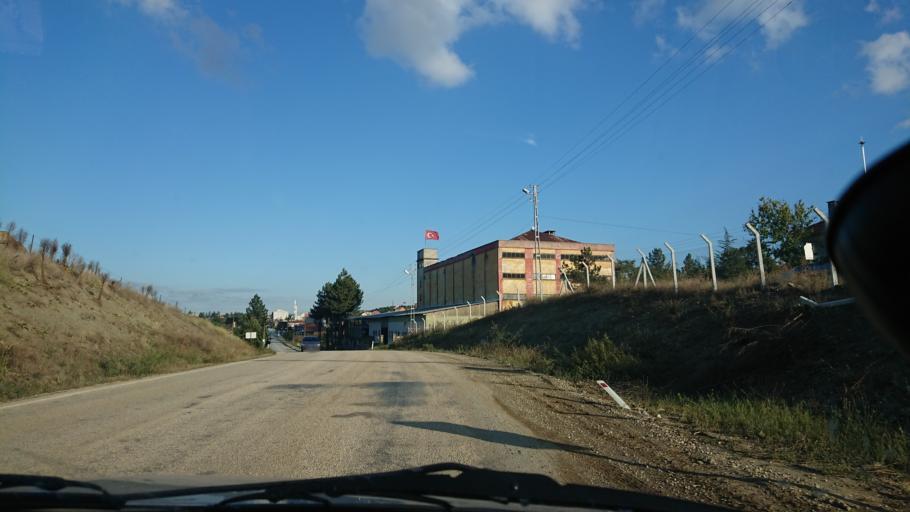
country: TR
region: Bilecik
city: Pazaryeri
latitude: 39.9998
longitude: 29.8876
